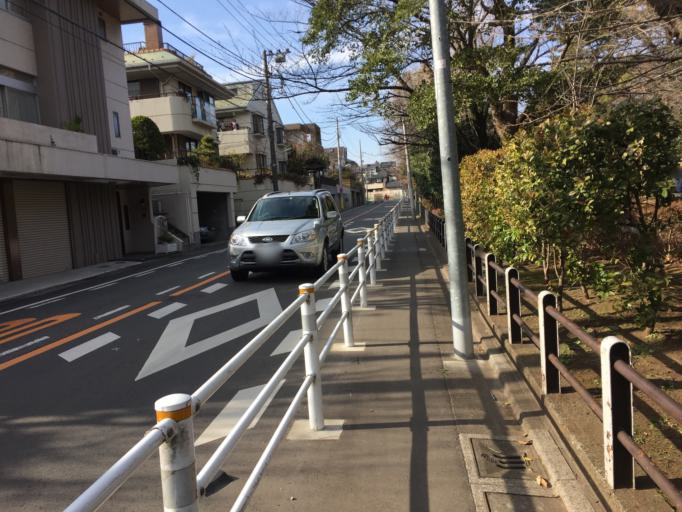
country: JP
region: Kanagawa
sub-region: Kawasaki-shi
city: Kawasaki
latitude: 35.5940
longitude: 139.6640
